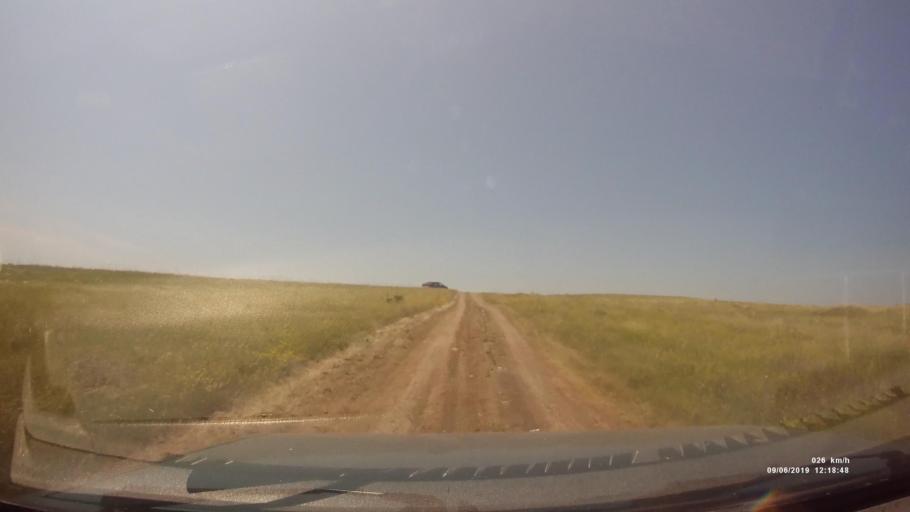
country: RU
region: Rostov
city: Kamensk-Shakhtinskiy
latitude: 48.2542
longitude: 40.3084
